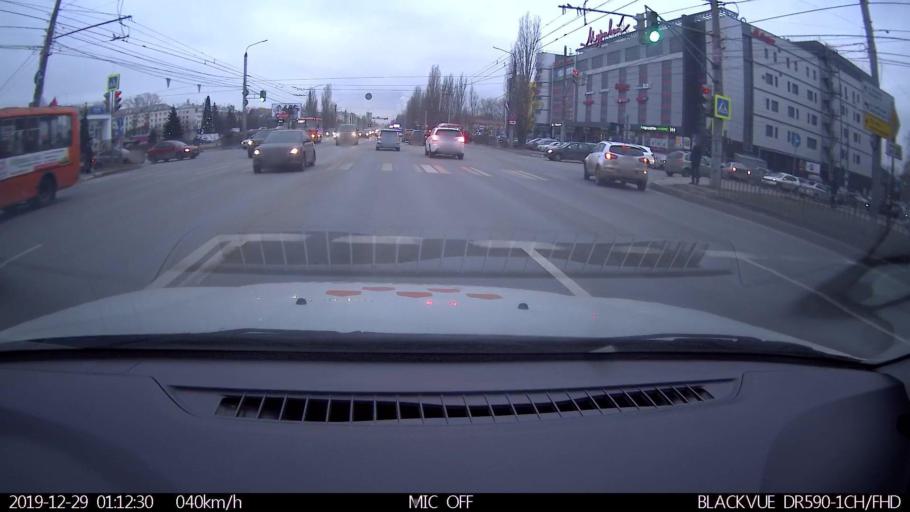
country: RU
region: Nizjnij Novgorod
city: Nizhniy Novgorod
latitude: 56.2856
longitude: 43.9315
